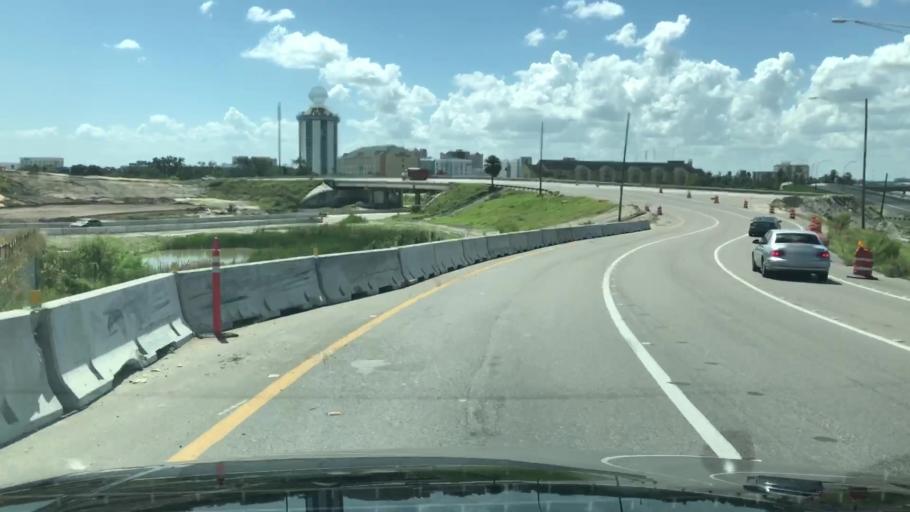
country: US
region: Florida
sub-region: Orange County
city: Tangelo Park
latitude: 28.4691
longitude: -81.4596
